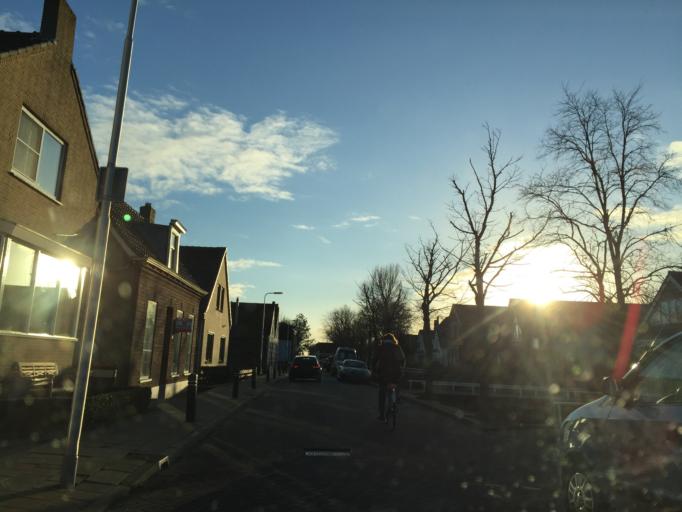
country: NL
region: South Holland
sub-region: Gemeente Lansingerland
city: Bleiswijk
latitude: 52.0136
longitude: 4.5315
